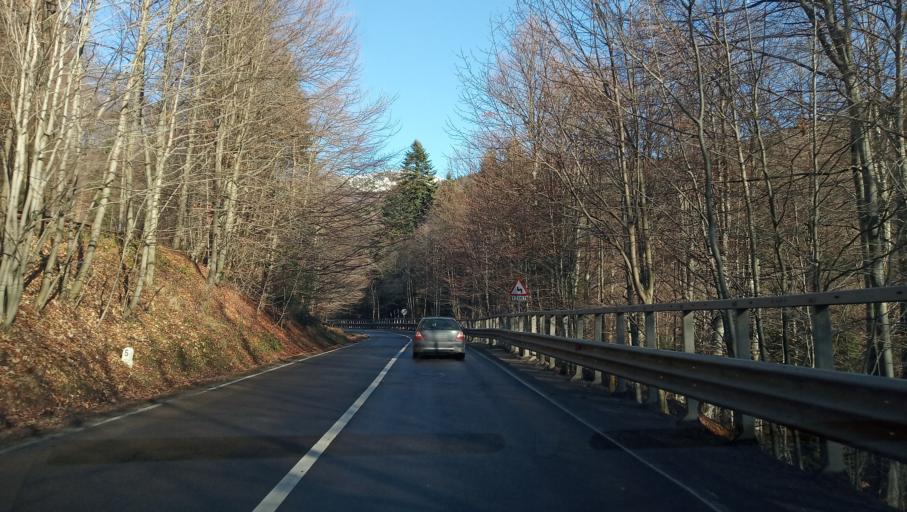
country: RO
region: Brasov
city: Crivina
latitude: 45.4699
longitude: 25.9317
